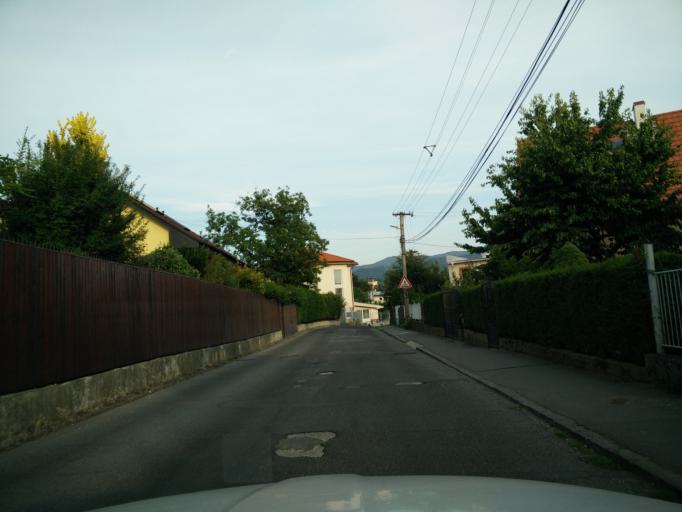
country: SK
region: Nitriansky
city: Prievidza
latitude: 48.7733
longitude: 18.6270
